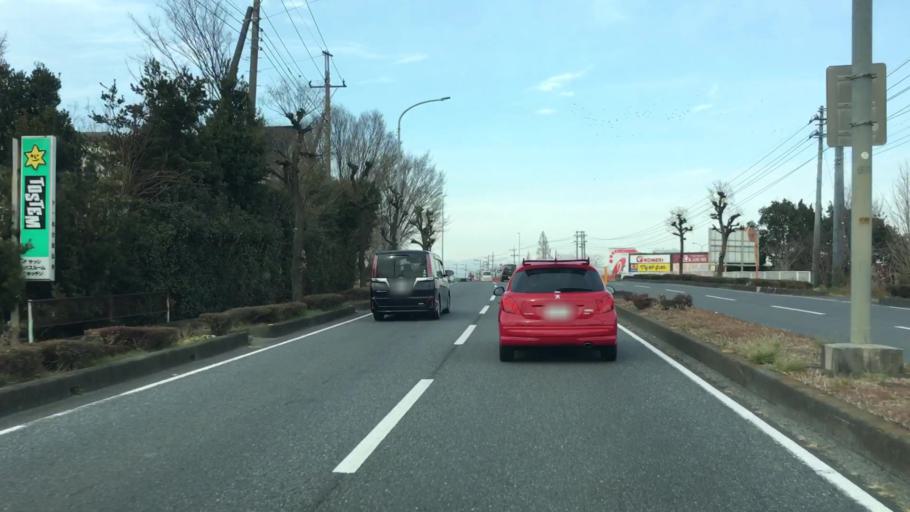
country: JP
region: Saitama
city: Menuma
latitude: 36.2069
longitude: 139.3706
